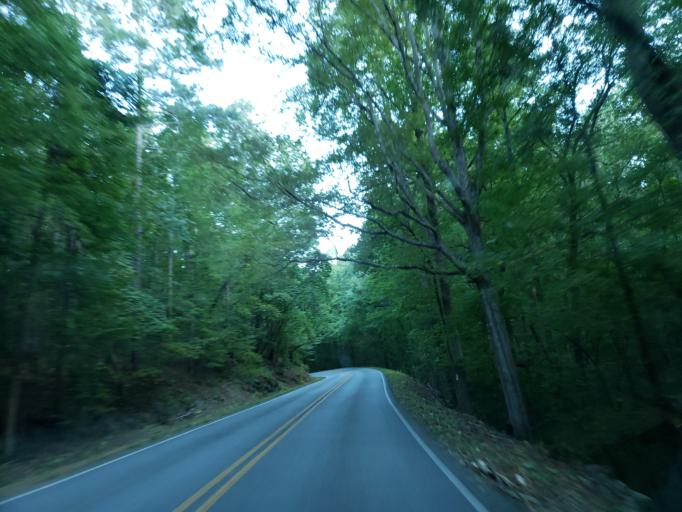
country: US
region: Georgia
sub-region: Bartow County
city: Rydal
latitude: 34.3615
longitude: -84.5797
